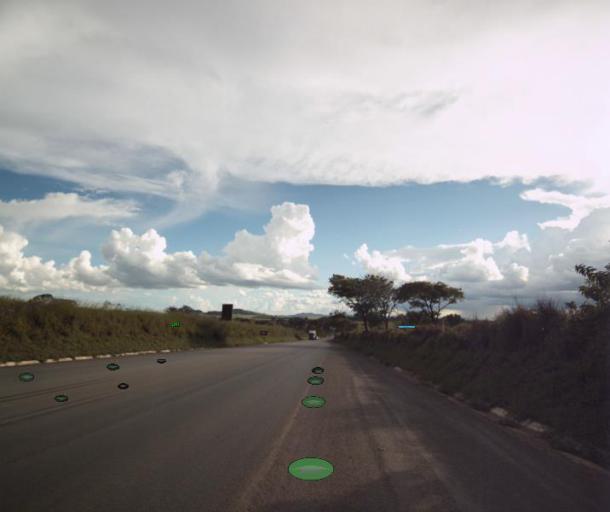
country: BR
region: Goias
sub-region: Itapaci
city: Itapaci
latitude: -15.1107
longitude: -49.4880
